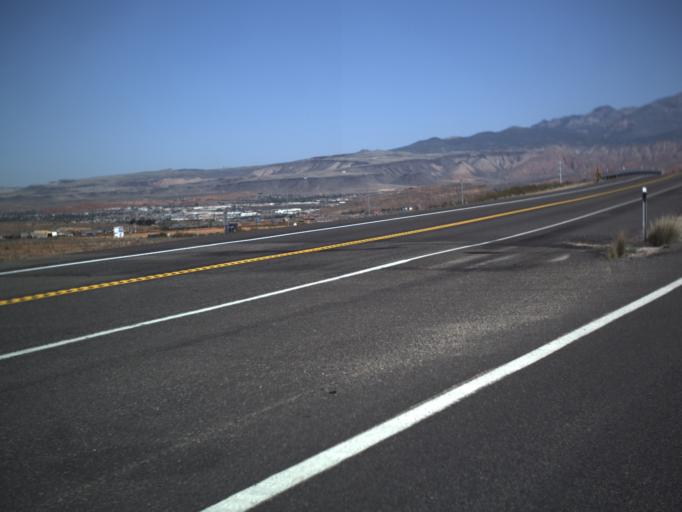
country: US
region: Utah
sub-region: Washington County
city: Washington
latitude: 37.0567
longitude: -113.4856
